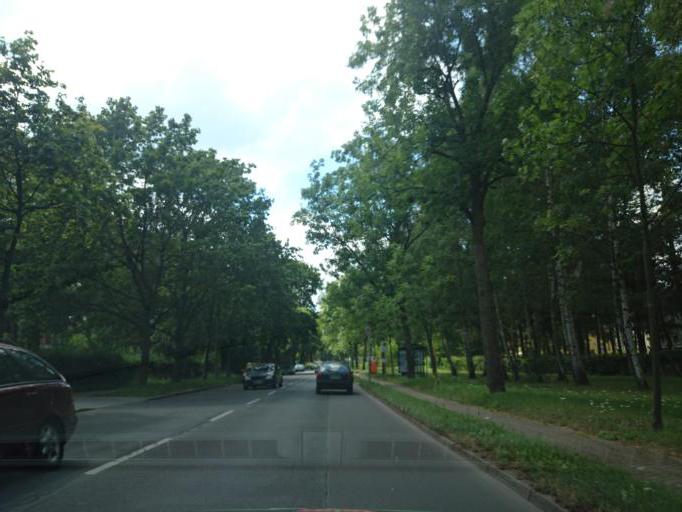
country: DE
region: Berlin
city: Gatow
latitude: 52.4674
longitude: 13.1656
